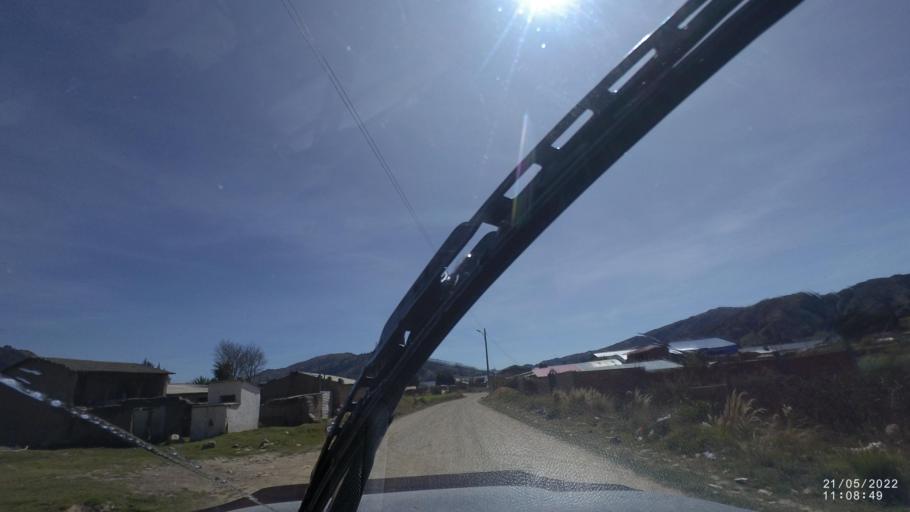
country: BO
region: Cochabamba
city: Colomi
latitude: -17.3037
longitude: -65.9113
